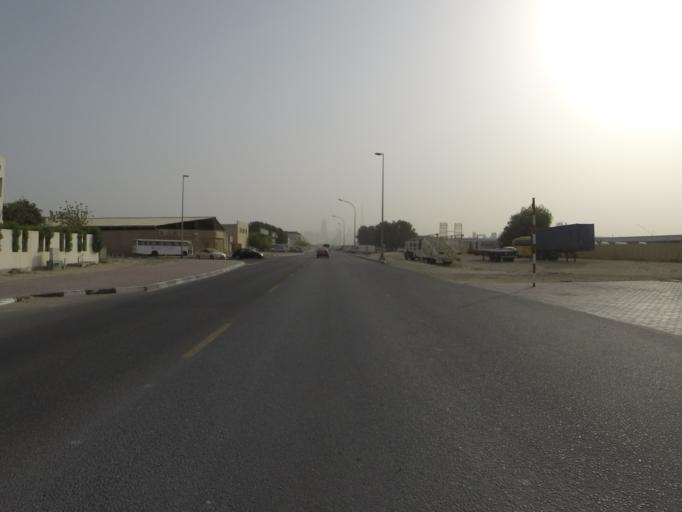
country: AE
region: Dubai
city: Dubai
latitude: 25.1506
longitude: 55.2301
